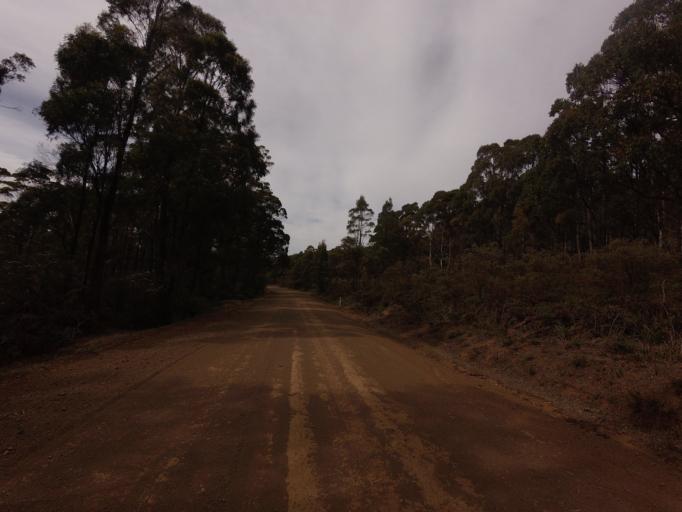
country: AU
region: Tasmania
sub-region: Sorell
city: Sorell
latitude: -42.4896
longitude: 147.6208
